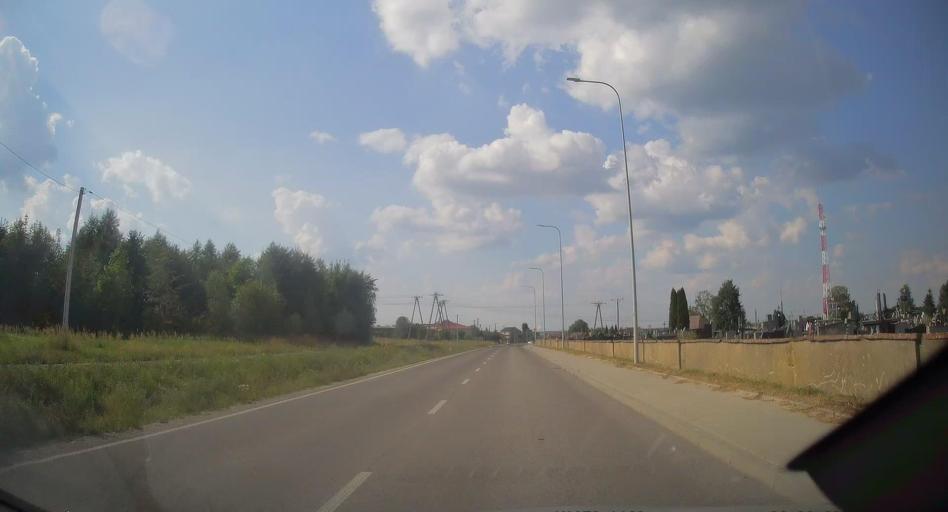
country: PL
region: Swietokrzyskie
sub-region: Powiat konecki
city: Radoszyce
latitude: 51.0686
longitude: 20.2700
